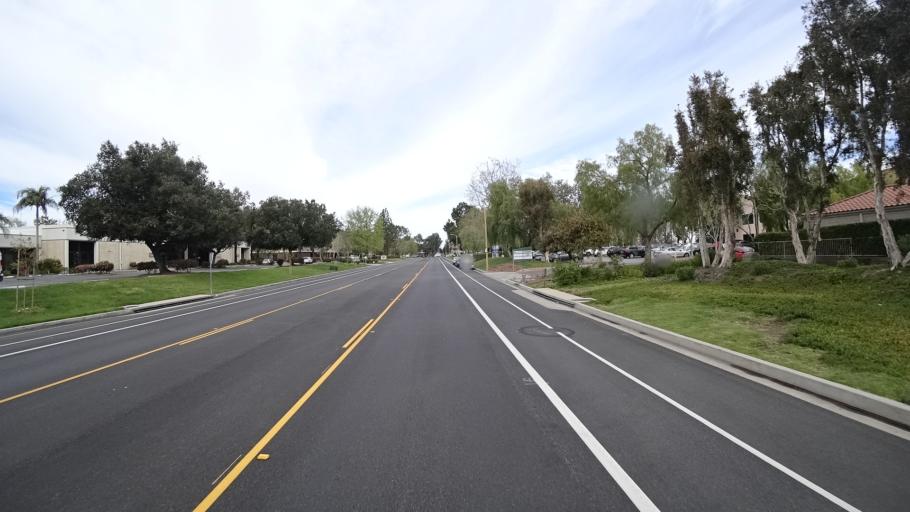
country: US
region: California
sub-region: Ventura County
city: Thousand Oaks
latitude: 34.1593
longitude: -118.8315
